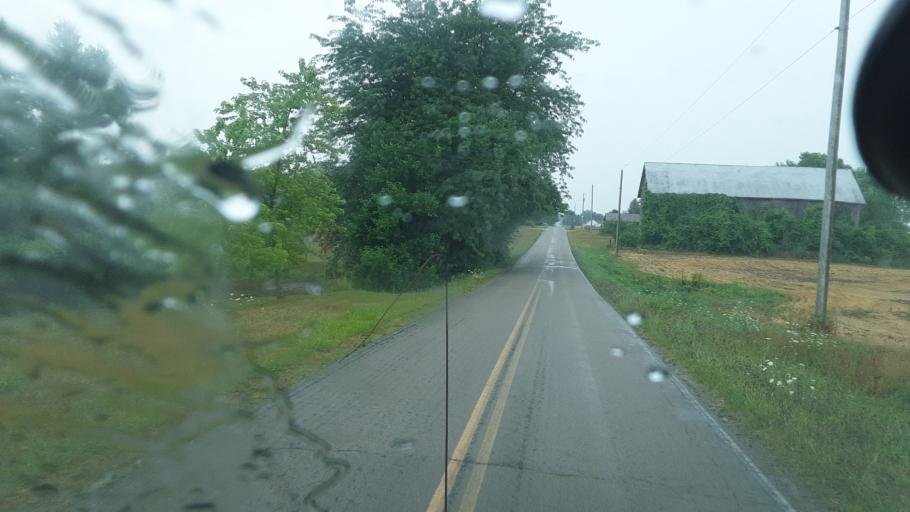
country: US
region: Ohio
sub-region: Williams County
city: Edgerton
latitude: 41.4261
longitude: -84.7849
